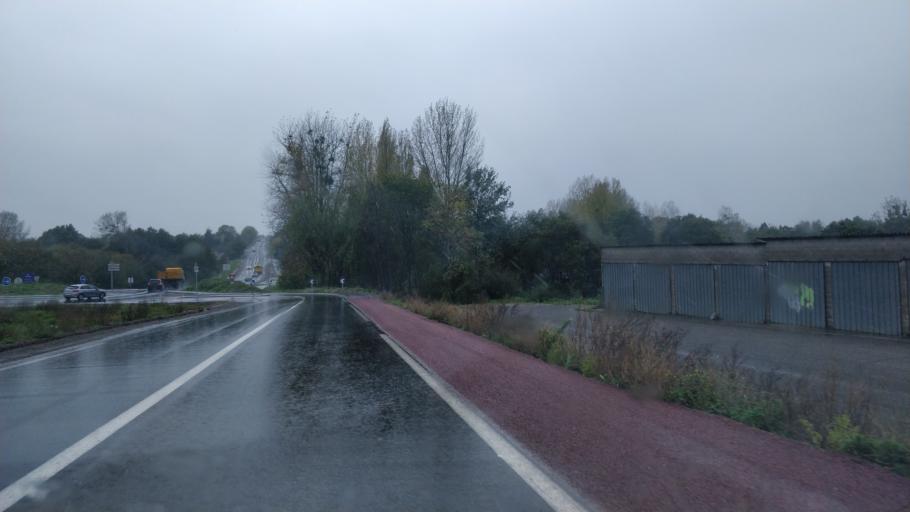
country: FR
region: Lower Normandy
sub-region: Departement de la Manche
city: Brehal
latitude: 48.8896
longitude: -1.5206
